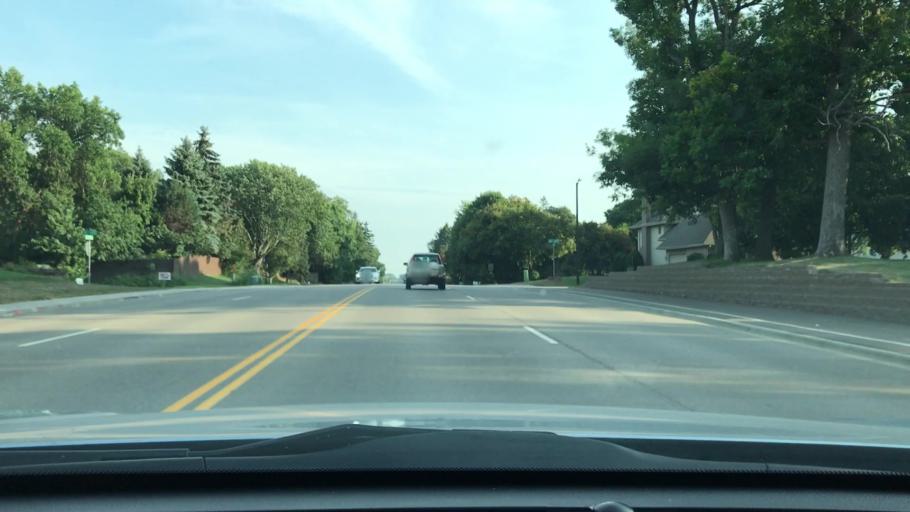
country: US
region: Minnesota
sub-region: Hennepin County
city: Plymouth
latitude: 45.0388
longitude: -93.4818
